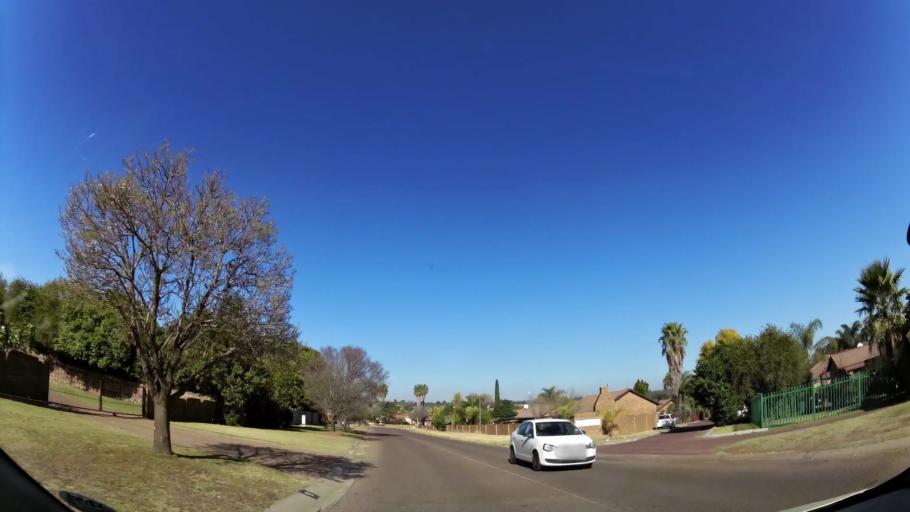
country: ZA
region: Mpumalanga
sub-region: Nkangala District Municipality
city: Witbank
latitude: -25.8878
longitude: 29.2485
